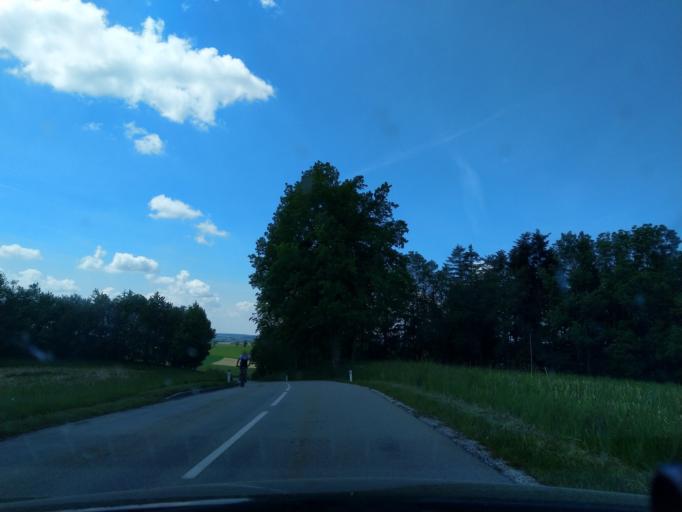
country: AT
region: Upper Austria
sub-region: Politischer Bezirk Ried im Innkreis
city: Ried im Innkreis
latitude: 48.2000
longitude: 13.5770
